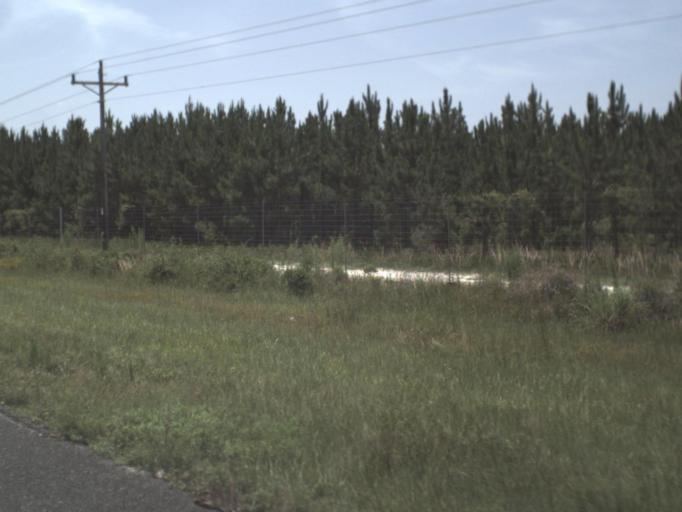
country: US
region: Florida
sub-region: Taylor County
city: Steinhatchee
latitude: 29.8055
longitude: -83.3417
